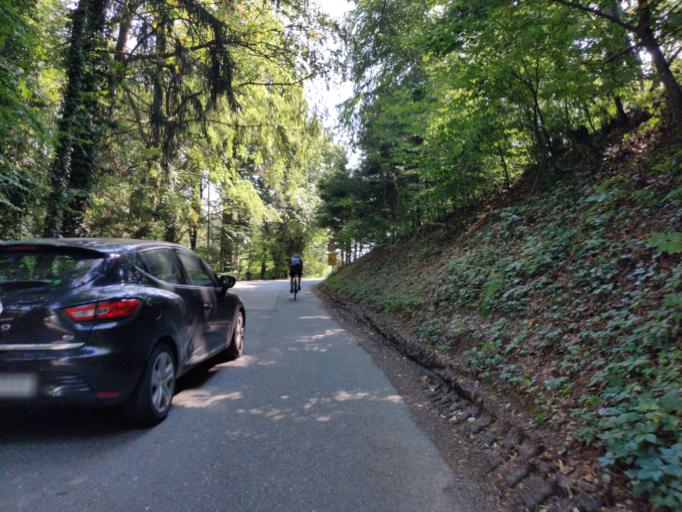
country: AT
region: Styria
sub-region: Politischer Bezirk Graz-Umgebung
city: Kumberg
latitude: 47.1352
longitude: 15.5262
